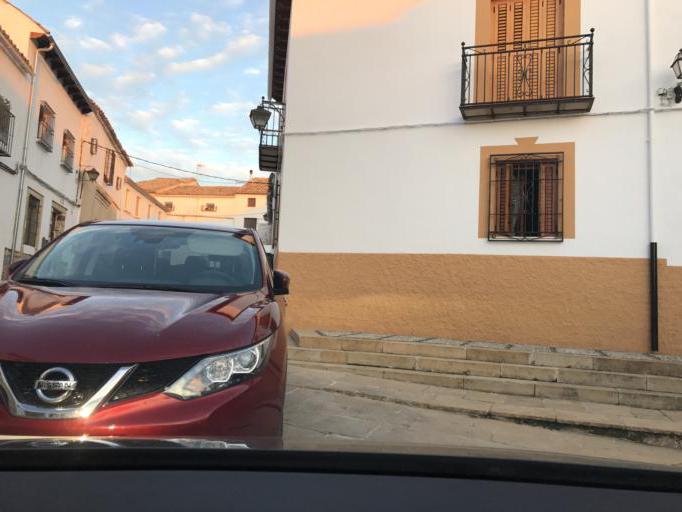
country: ES
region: Andalusia
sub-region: Provincia de Jaen
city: Ubeda
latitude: 38.0064
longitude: -3.3682
